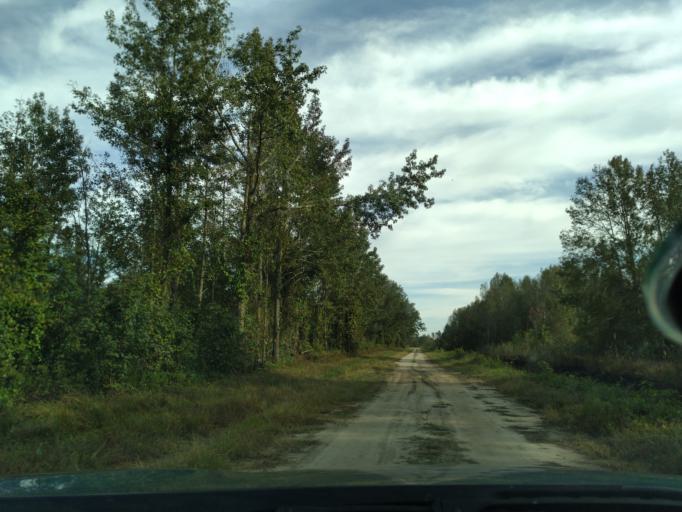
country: US
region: North Carolina
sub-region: Beaufort County
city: Belhaven
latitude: 35.6927
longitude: -76.5541
